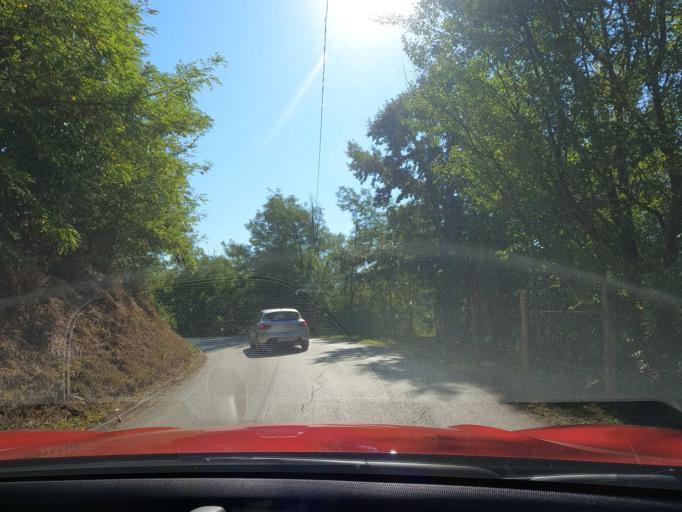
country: RS
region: Central Serbia
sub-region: Raski Okrug
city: Kraljevo
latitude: 43.7698
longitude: 20.6618
